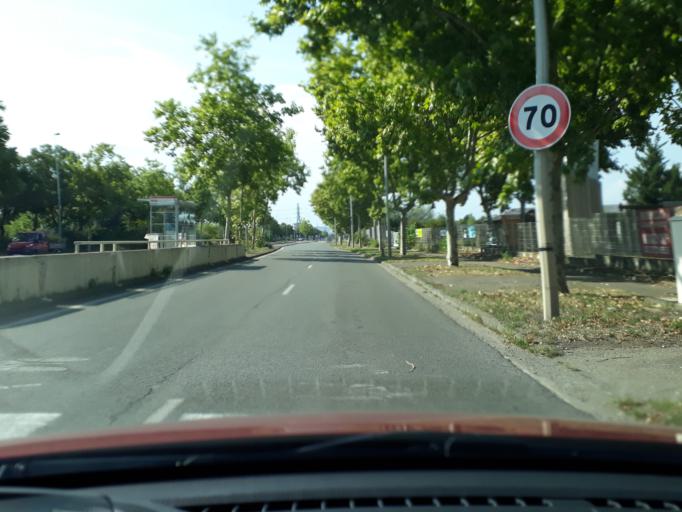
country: FR
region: Rhone-Alpes
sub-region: Departement du Rhone
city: Saint-Priest
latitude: 45.7019
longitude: 4.9174
